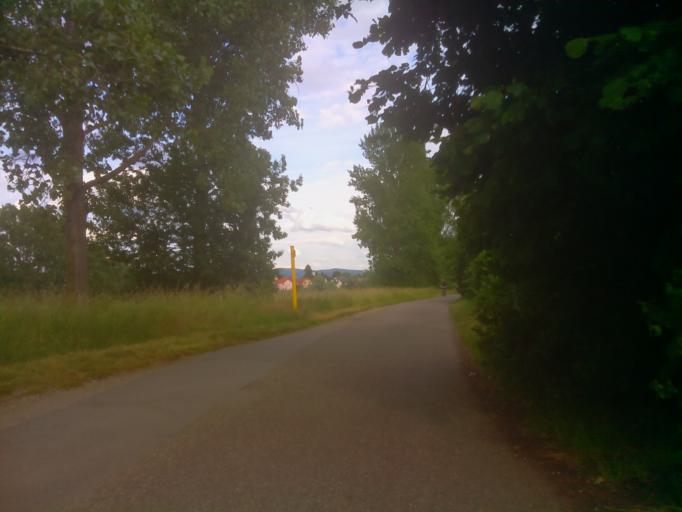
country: DE
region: Baden-Wuerttemberg
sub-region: Karlsruhe Region
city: Ilvesheim
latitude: 49.4748
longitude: 8.5556
